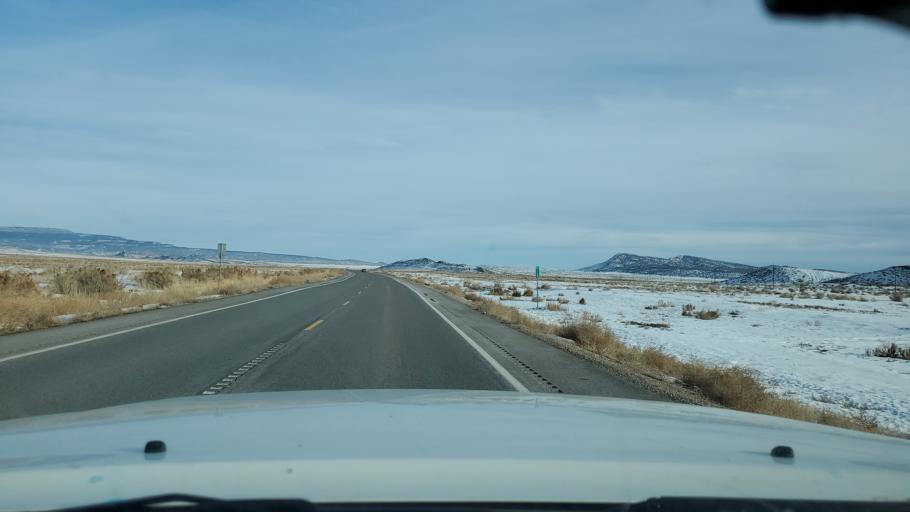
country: US
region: Utah
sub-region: Uintah County
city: Naples
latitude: 40.2931
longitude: -109.1726
